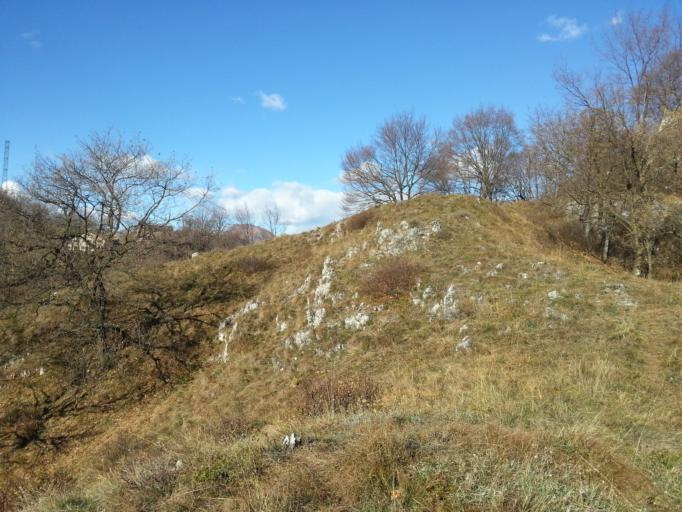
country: IT
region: Lombardy
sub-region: Provincia di Como
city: Griante
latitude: 46.0055
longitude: 9.2223
